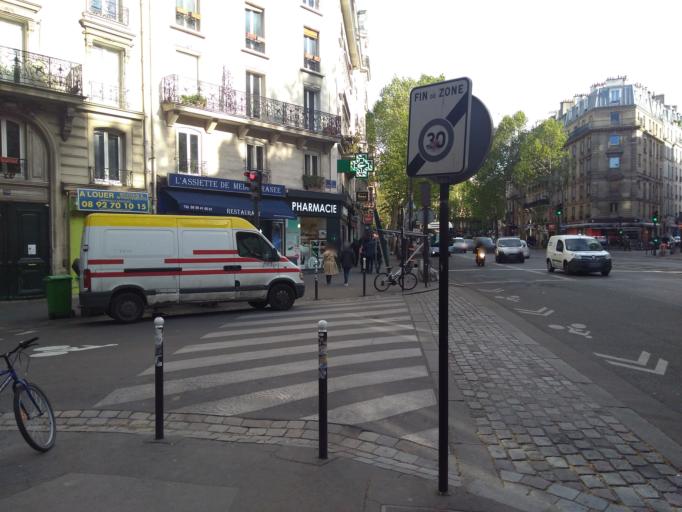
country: FR
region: Ile-de-France
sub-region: Paris
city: Saint-Ouen
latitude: 48.8928
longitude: 2.3488
